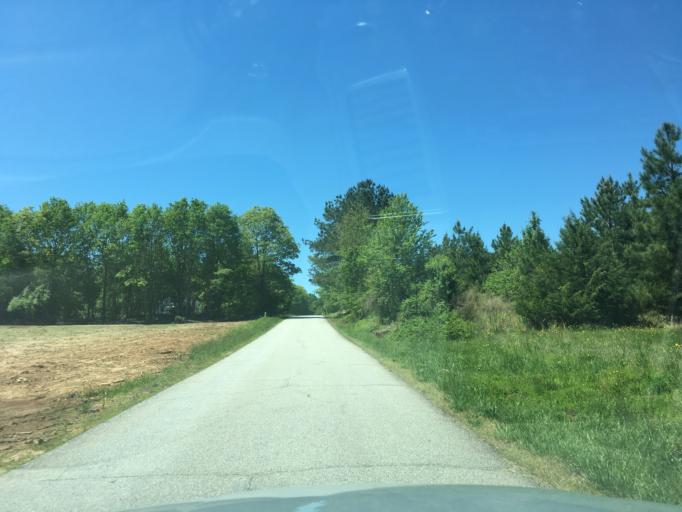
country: US
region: South Carolina
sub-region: Spartanburg County
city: Duncan
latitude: 34.8780
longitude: -82.1773
